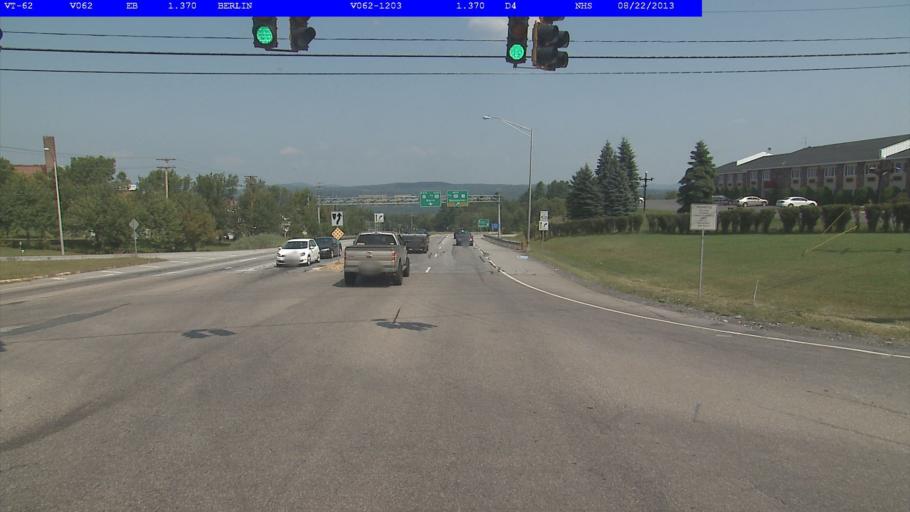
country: US
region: Vermont
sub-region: Washington County
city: Montpelier
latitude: 44.2183
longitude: -72.5598
